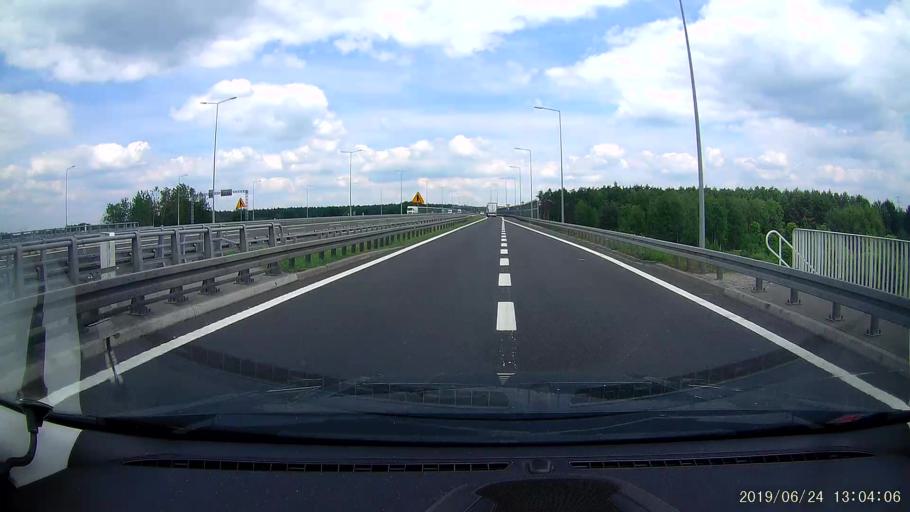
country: PL
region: Silesian Voivodeship
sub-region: Zory
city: Zory
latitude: 50.0780
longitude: 18.6637
